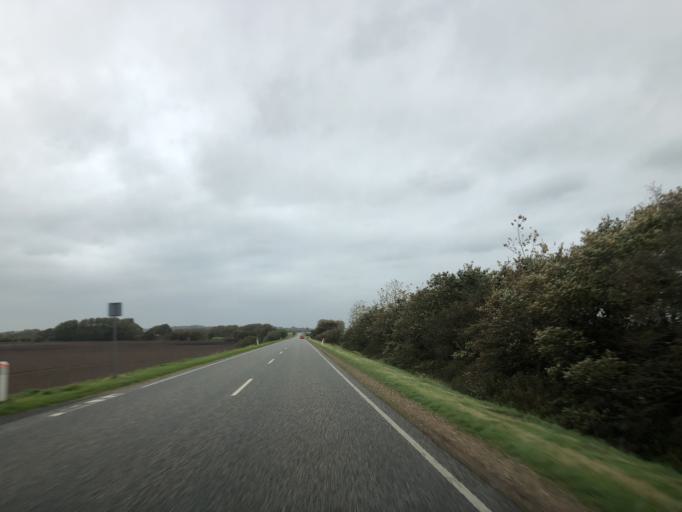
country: DK
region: Central Jutland
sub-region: Herning Kommune
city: Vildbjerg
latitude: 56.2071
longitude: 8.7274
